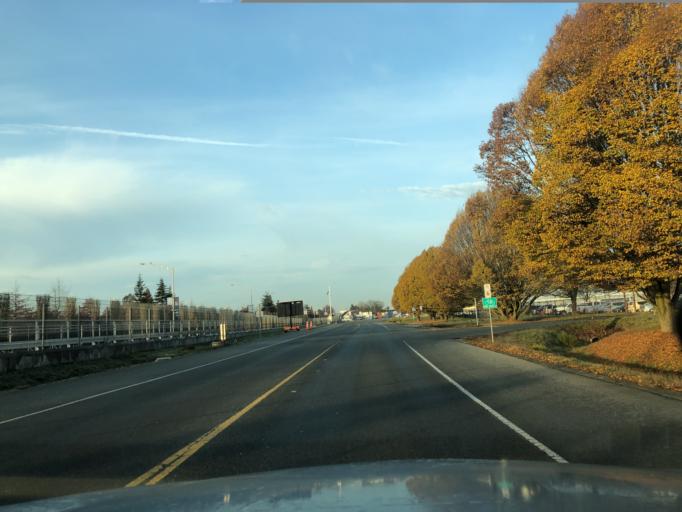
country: CA
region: British Columbia
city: Richmond
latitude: 49.1932
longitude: -123.1587
